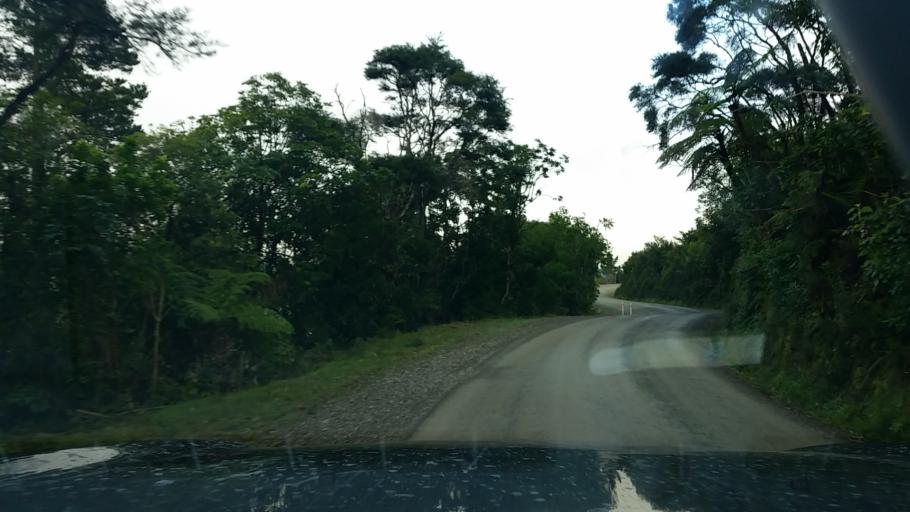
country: NZ
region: Marlborough
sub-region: Marlborough District
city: Picton
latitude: -41.1784
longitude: 174.0642
